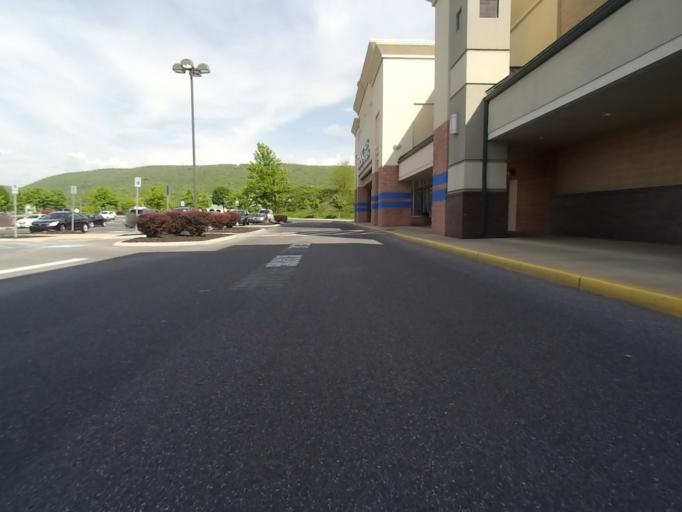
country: US
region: Pennsylvania
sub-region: Centre County
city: Houserville
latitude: 40.8307
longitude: -77.8078
